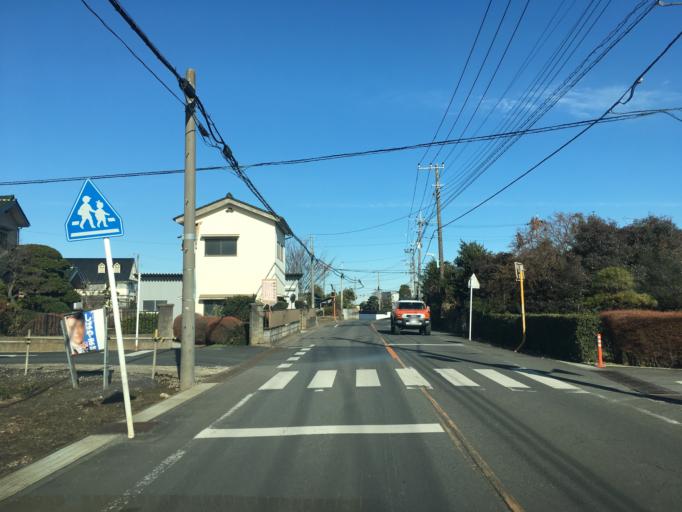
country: JP
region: Saitama
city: Sayama
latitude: 35.7998
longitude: 139.3962
